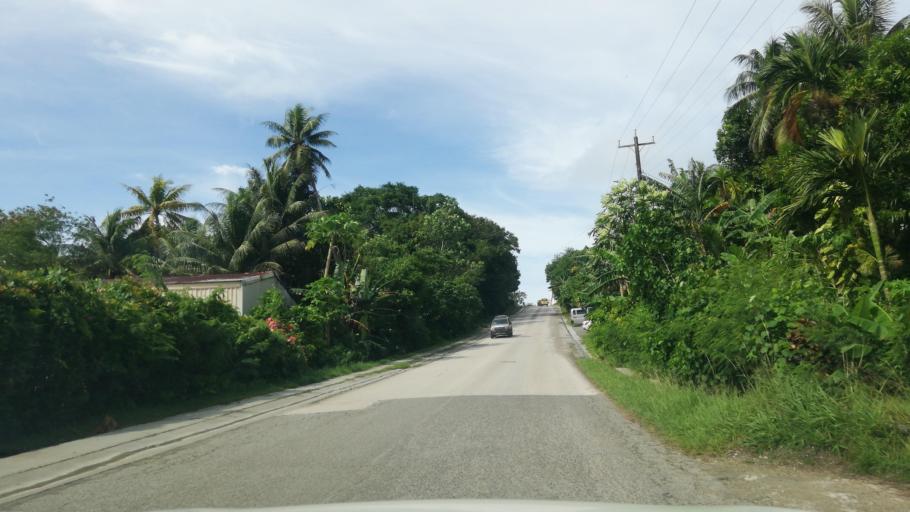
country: FM
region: Yap
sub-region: Weloy Municipality
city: Colonia
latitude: 9.5161
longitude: 138.1141
